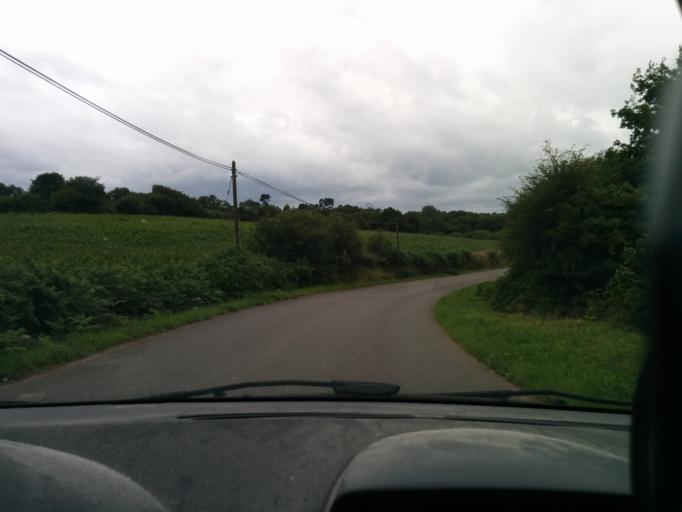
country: FR
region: Brittany
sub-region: Departement du Finistere
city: Brasparts
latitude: 48.3531
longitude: -3.9765
